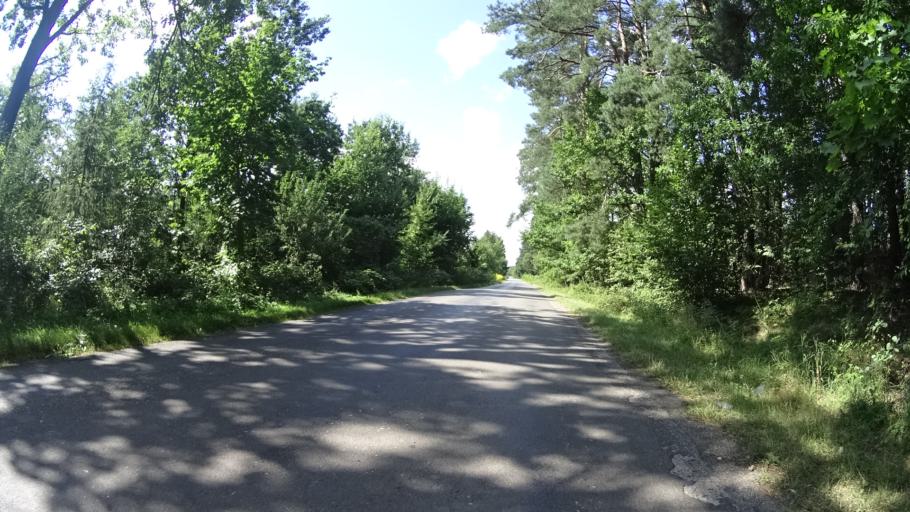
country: PL
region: Masovian Voivodeship
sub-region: Powiat grojecki
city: Mogielnica
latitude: 51.6931
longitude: 20.7355
